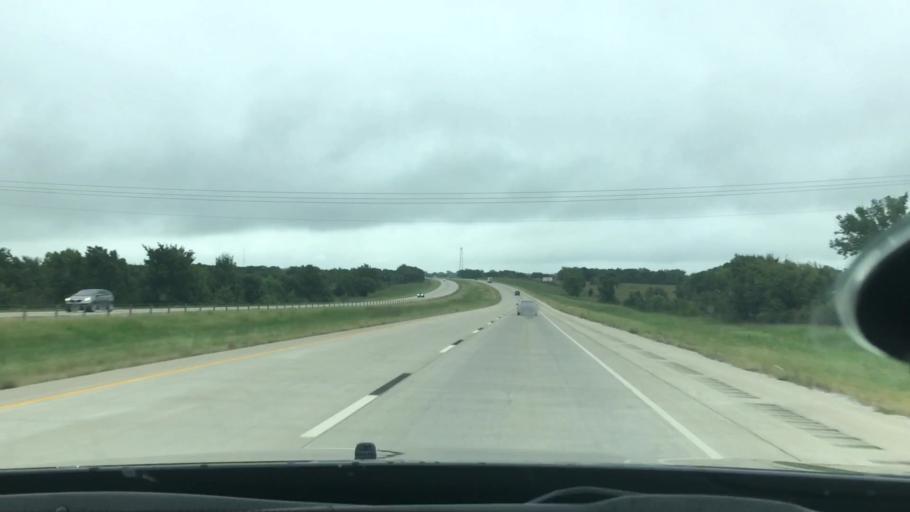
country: US
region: Oklahoma
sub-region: Okmulgee County
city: Wilson
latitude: 35.4275
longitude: -96.0709
